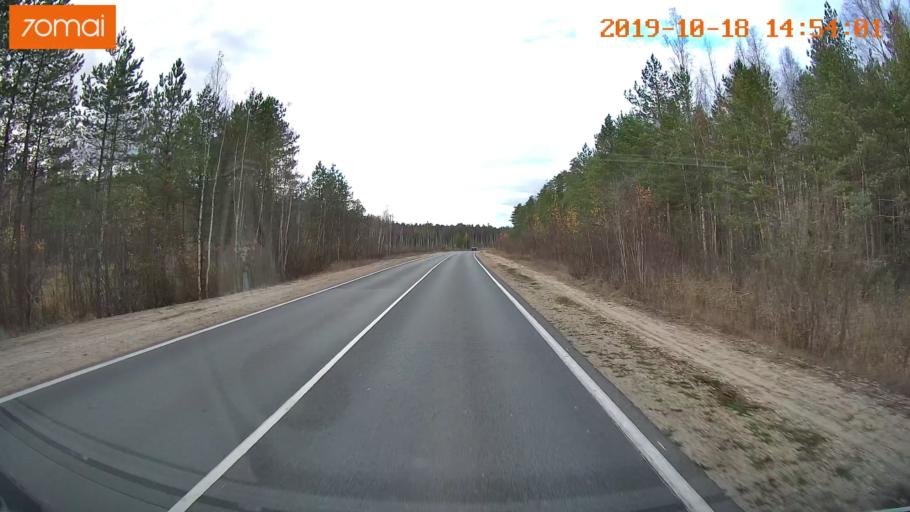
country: RU
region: Vladimir
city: Kurlovo
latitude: 55.4358
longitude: 40.6060
